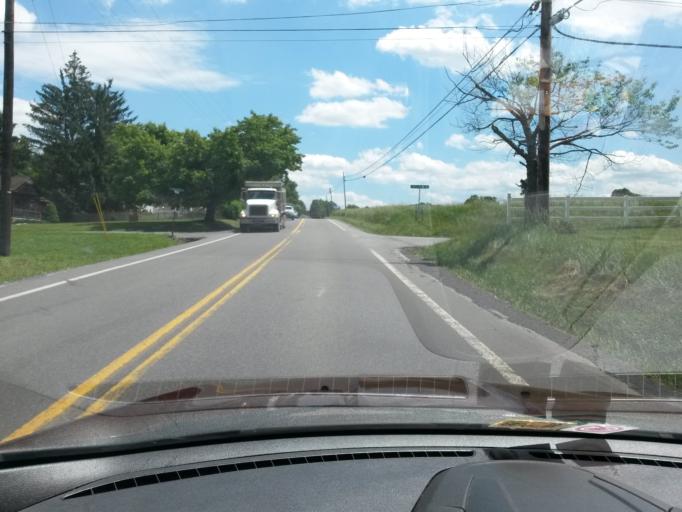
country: US
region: West Virginia
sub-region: Greenbrier County
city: Rainelle
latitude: 37.9295
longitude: -80.6507
